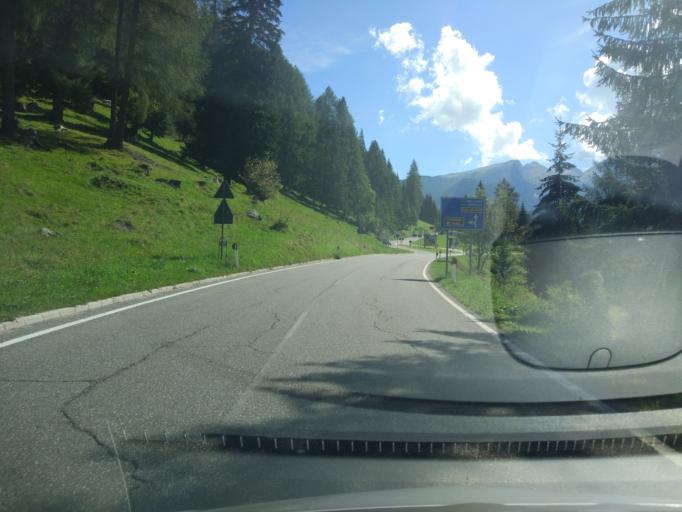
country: IT
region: Trentino-Alto Adige
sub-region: Provincia di Trento
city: Moena
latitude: 46.3108
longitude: 11.6801
